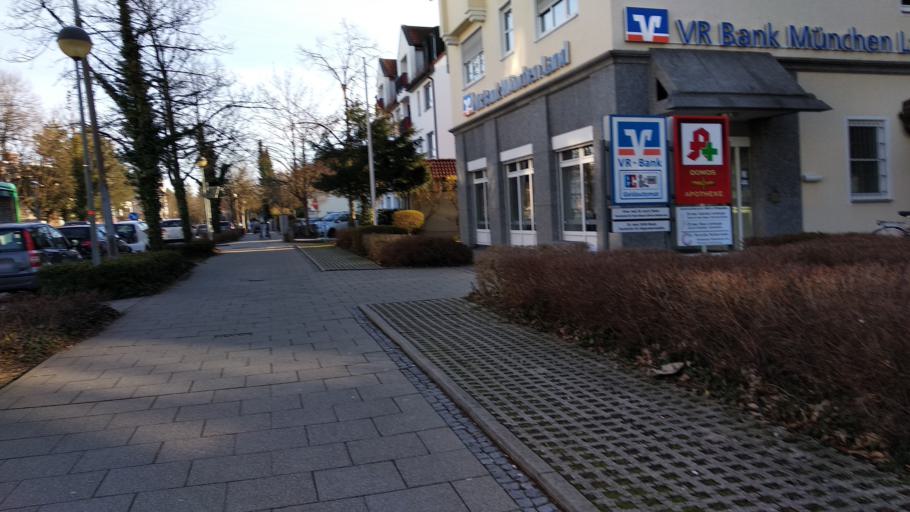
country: DE
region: Bavaria
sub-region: Upper Bavaria
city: Unterhaching
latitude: 48.0642
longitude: 11.6135
